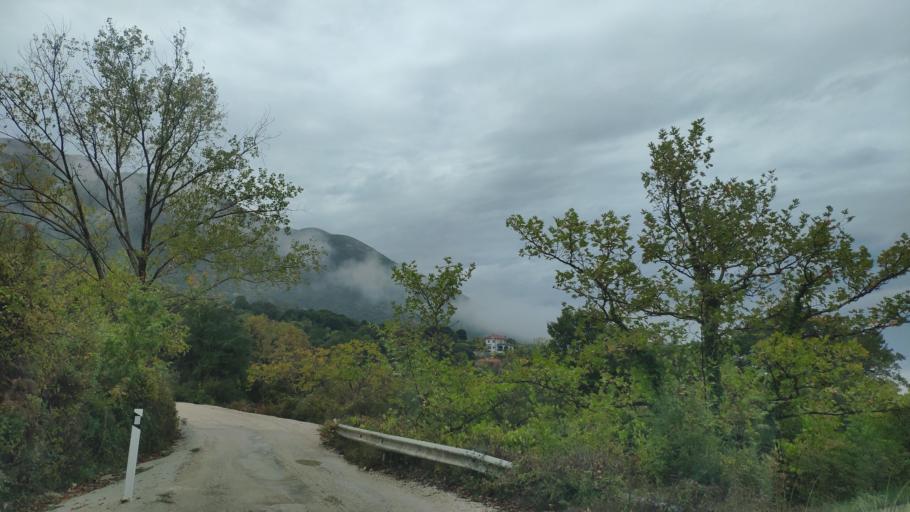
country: GR
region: Epirus
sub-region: Nomos Thesprotias
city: Paramythia
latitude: 39.4596
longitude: 20.6782
